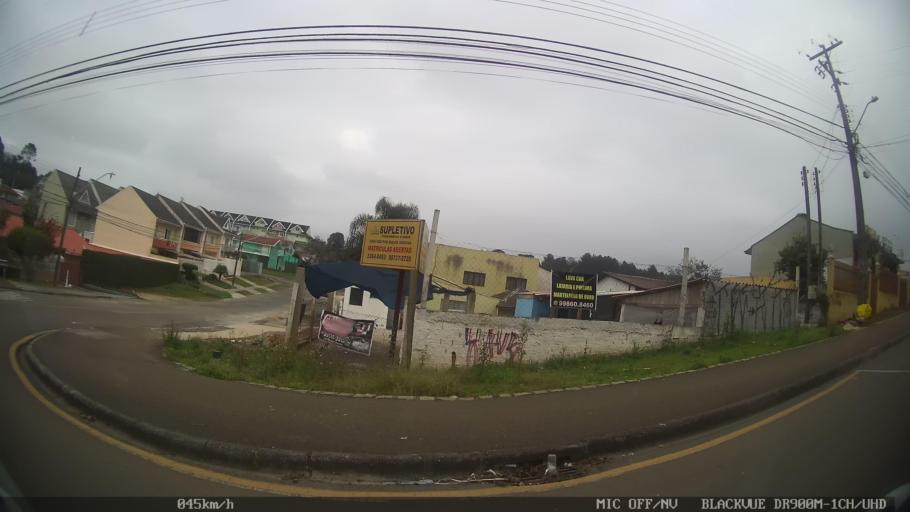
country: BR
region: Parana
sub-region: Almirante Tamandare
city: Almirante Tamandare
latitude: -25.3842
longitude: -49.3348
